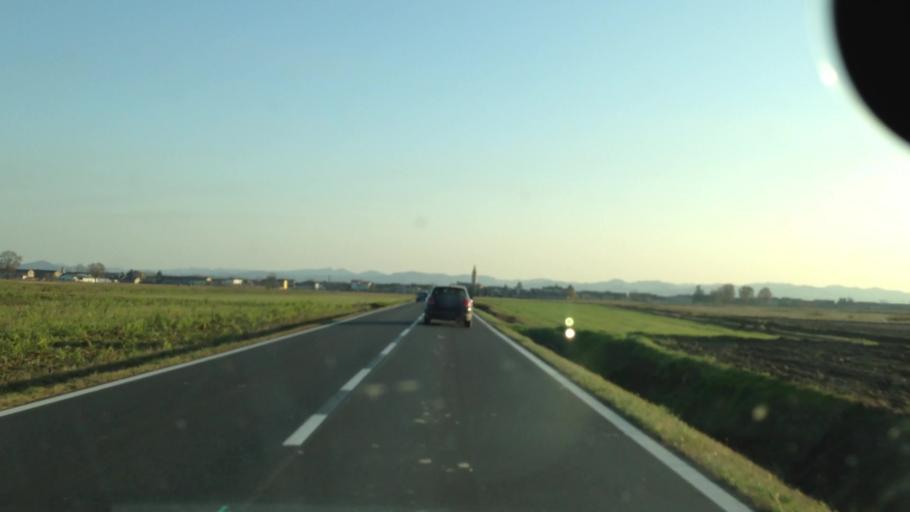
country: IT
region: Piedmont
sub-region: Provincia di Vercelli
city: Lamporo
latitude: 45.2395
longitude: 8.0932
